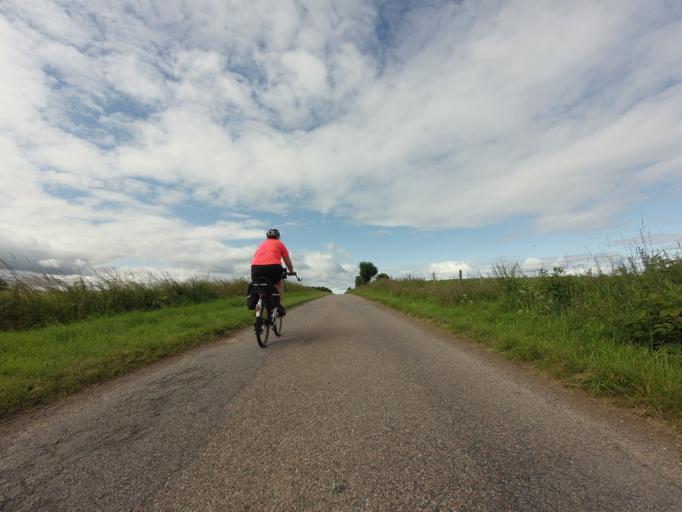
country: GB
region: Scotland
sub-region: Moray
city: Hopeman
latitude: 57.6647
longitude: -3.4274
